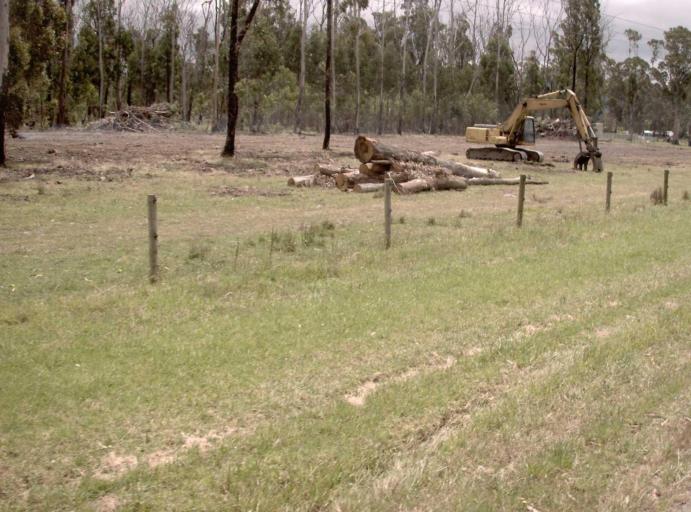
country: AU
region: Victoria
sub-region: Latrobe
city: Traralgon
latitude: -38.5327
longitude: 146.6583
